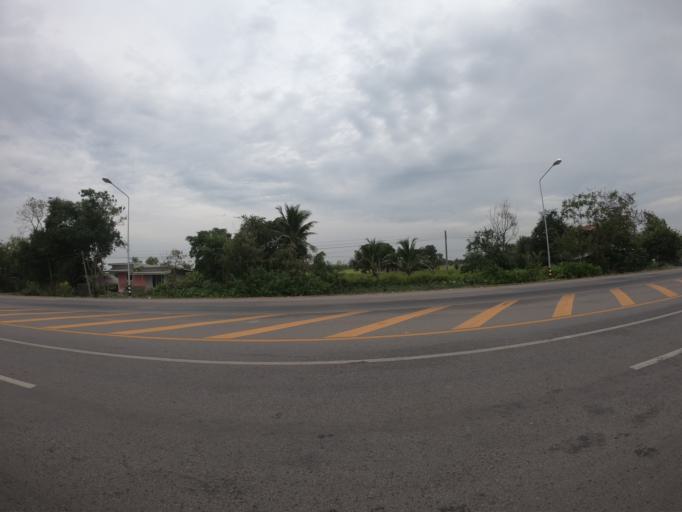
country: TH
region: Roi Et
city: Chiang Khwan
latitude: 16.1315
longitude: 103.8508
